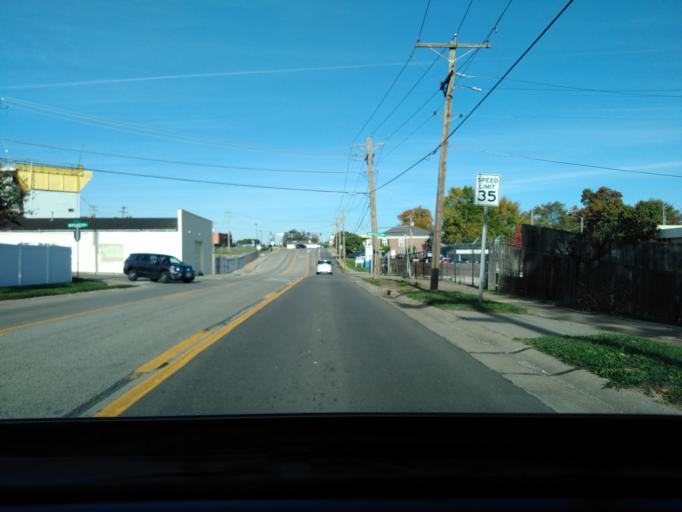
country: US
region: Missouri
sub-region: Saint Louis County
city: Concord
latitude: 38.5084
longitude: -90.3716
